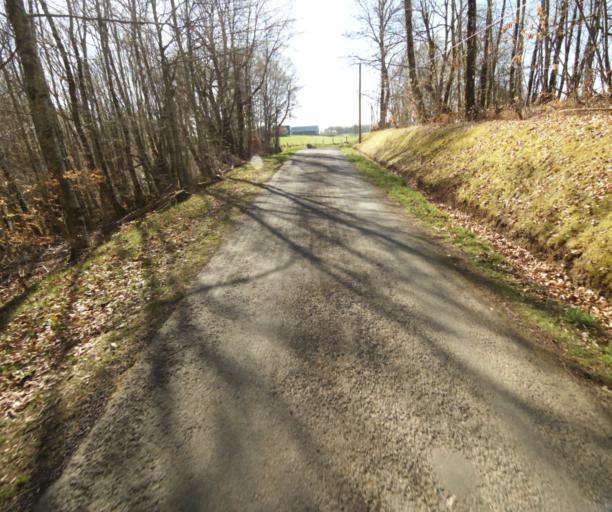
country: FR
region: Limousin
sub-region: Departement de la Correze
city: Seilhac
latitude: 45.3843
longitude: 1.7600
